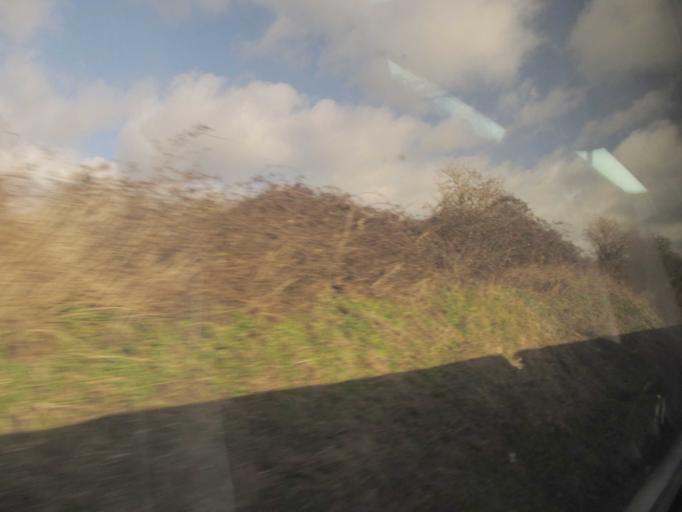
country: GB
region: England
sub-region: Royal Borough of Windsor and Maidenhead
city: White Waltham
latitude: 51.5007
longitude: -0.7856
